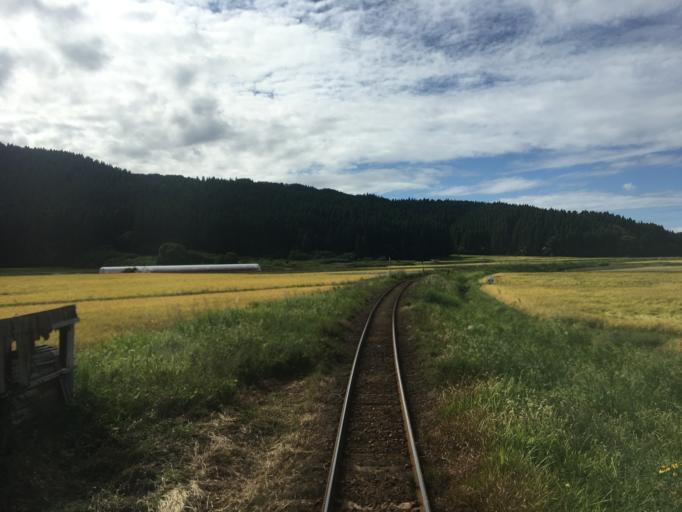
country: JP
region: Yamagata
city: Yuza
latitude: 39.3205
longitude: 140.0931
